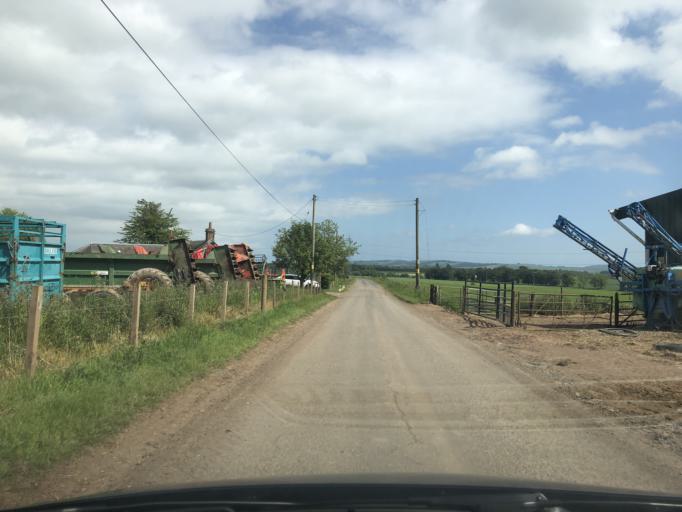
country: GB
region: Scotland
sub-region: Angus
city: Kirriemuir
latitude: 56.7214
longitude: -2.9556
